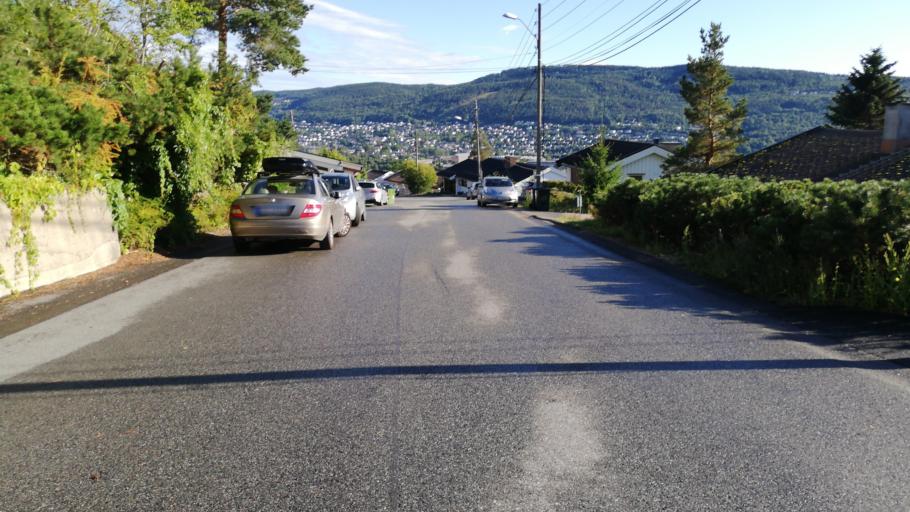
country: NO
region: Buskerud
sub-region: Drammen
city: Drammen
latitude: 59.7557
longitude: 10.1775
